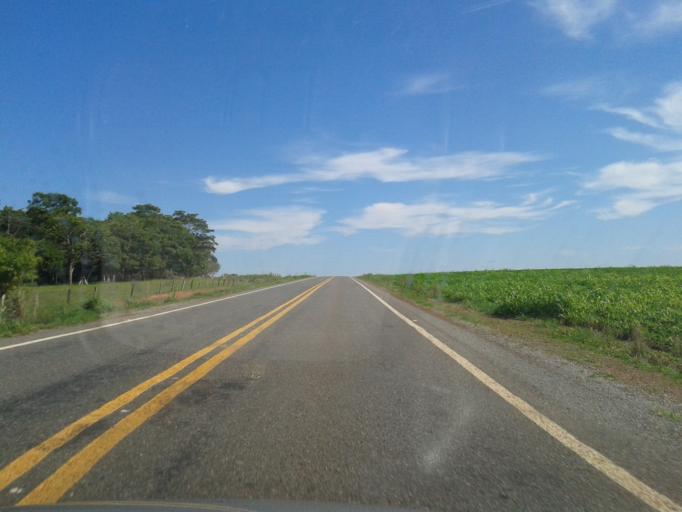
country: BR
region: Goias
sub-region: Piracanjuba
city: Piracanjuba
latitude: -17.3229
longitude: -48.8008
